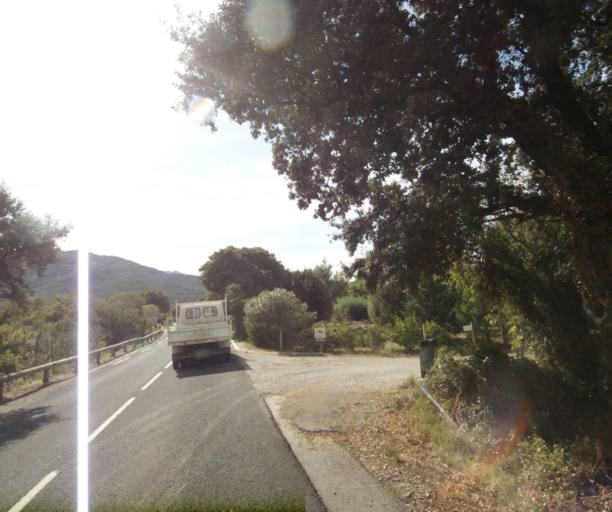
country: FR
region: Languedoc-Roussillon
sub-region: Departement des Pyrenees-Orientales
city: Sant Andreu de Sureda
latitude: 42.5334
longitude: 2.9897
